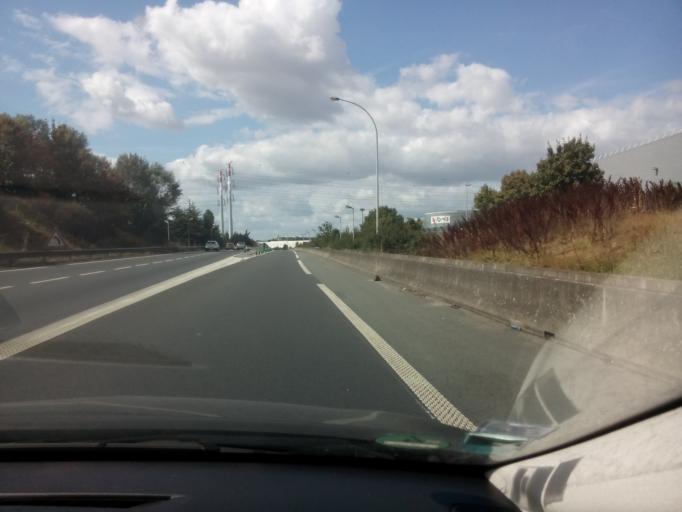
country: FR
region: Ile-de-France
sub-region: Departement du Val-de-Marne
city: Chevilly-Larue
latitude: 48.7571
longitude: 2.3407
